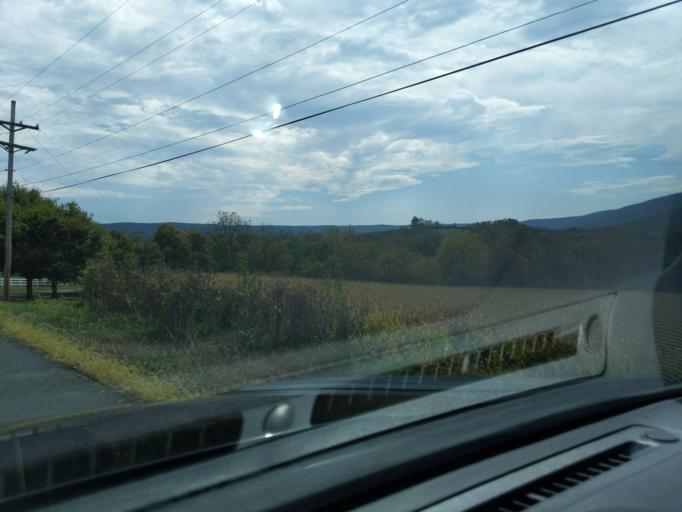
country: US
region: Pennsylvania
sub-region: Blair County
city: Hollidaysburg
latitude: 40.4269
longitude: -78.3491
